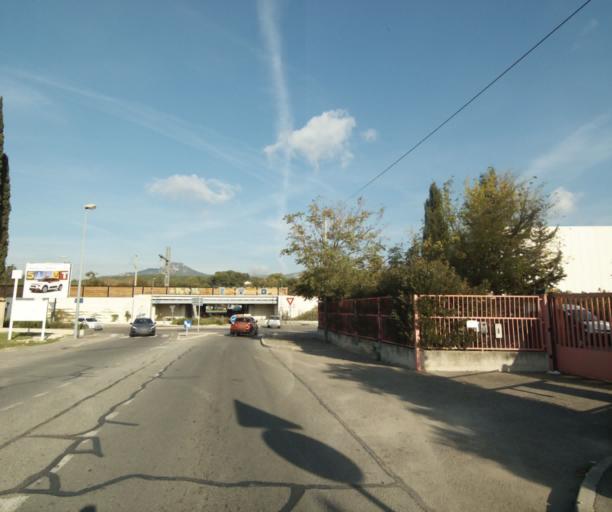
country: FR
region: Provence-Alpes-Cote d'Azur
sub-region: Departement des Bouches-du-Rhone
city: Aubagne
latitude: 43.2873
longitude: 5.5483
